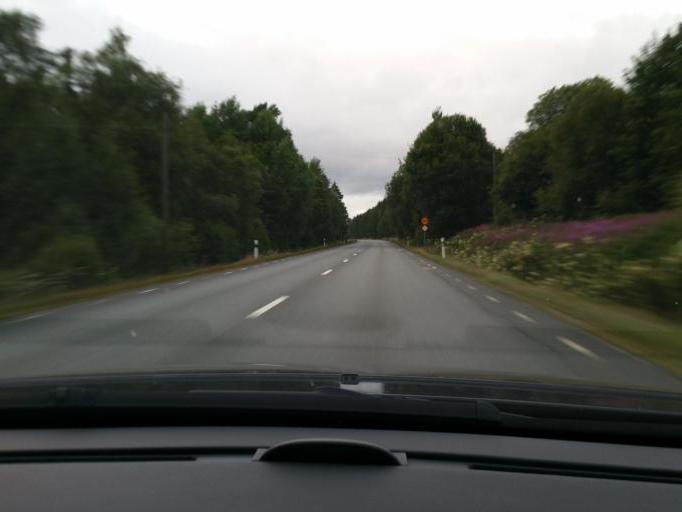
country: SE
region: Kronoberg
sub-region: Alvesta Kommun
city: Moheda
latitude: 57.0230
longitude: 14.5622
